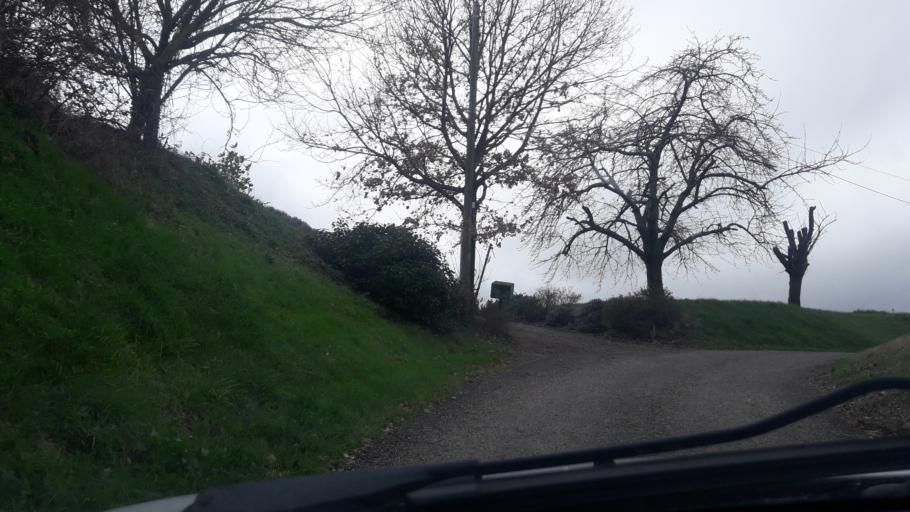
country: FR
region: Midi-Pyrenees
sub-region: Departement du Gers
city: Gimont
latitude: 43.6553
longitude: 0.9648
